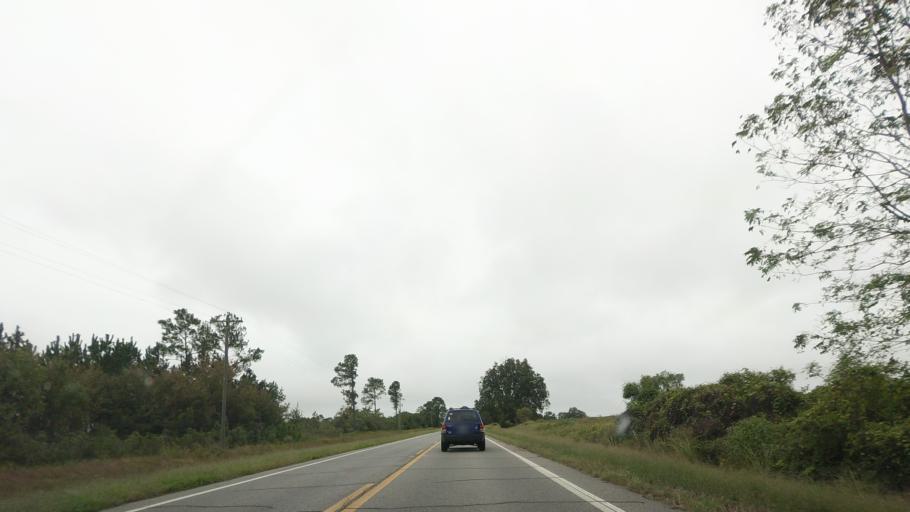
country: US
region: Georgia
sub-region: Irwin County
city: Ocilla
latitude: 31.5478
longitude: -83.2540
